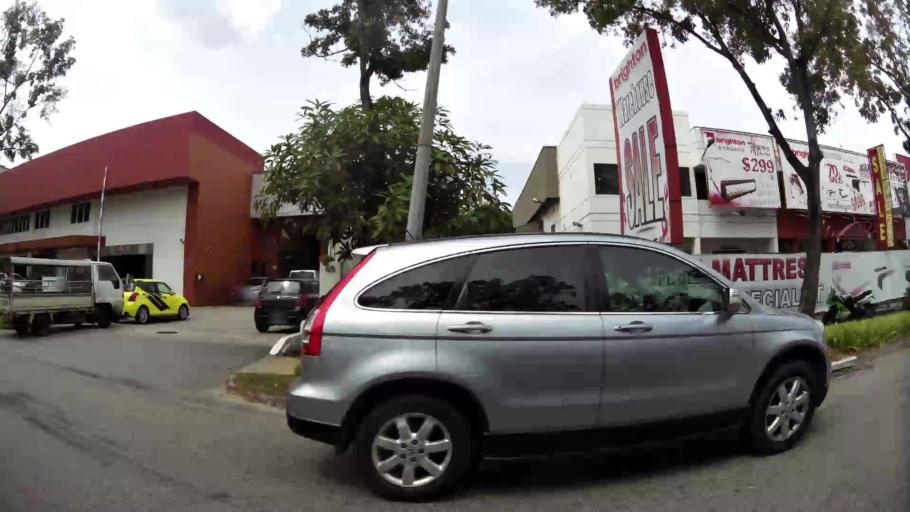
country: MY
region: Johor
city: Johor Bahru
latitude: 1.4083
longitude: 103.7491
